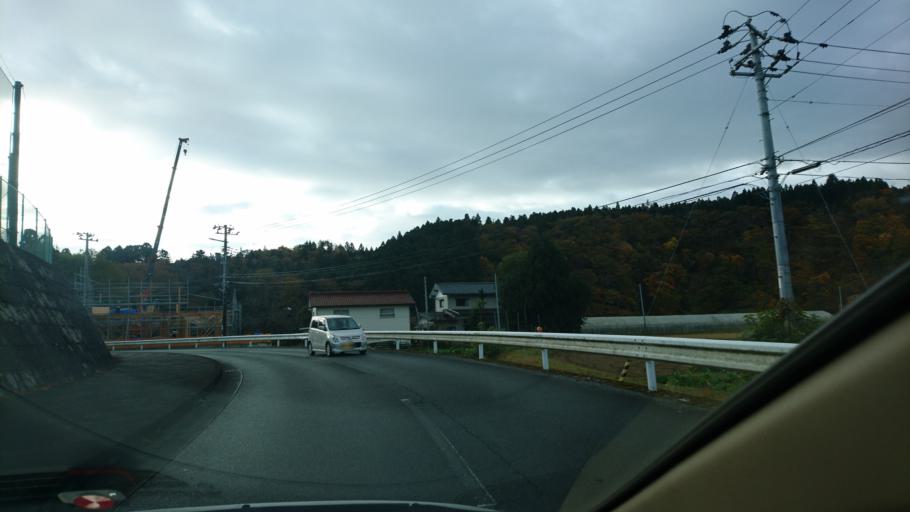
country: JP
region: Iwate
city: Ofunato
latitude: 38.9107
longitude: 141.5419
